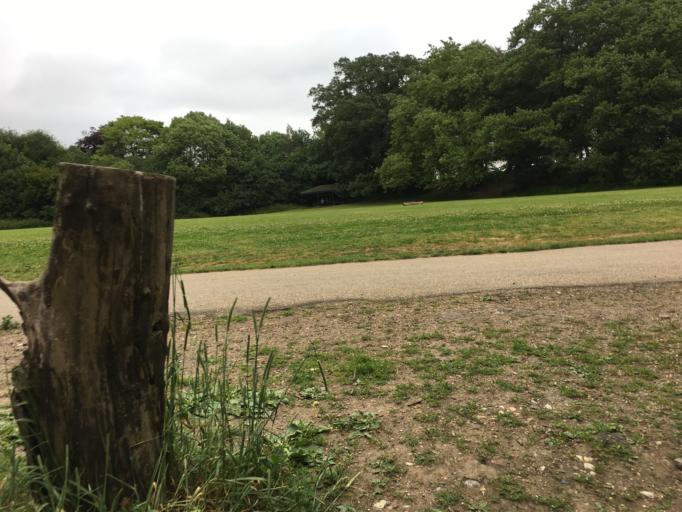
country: GB
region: England
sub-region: Greater London
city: Belsize Park
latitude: 51.5625
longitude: -0.1670
